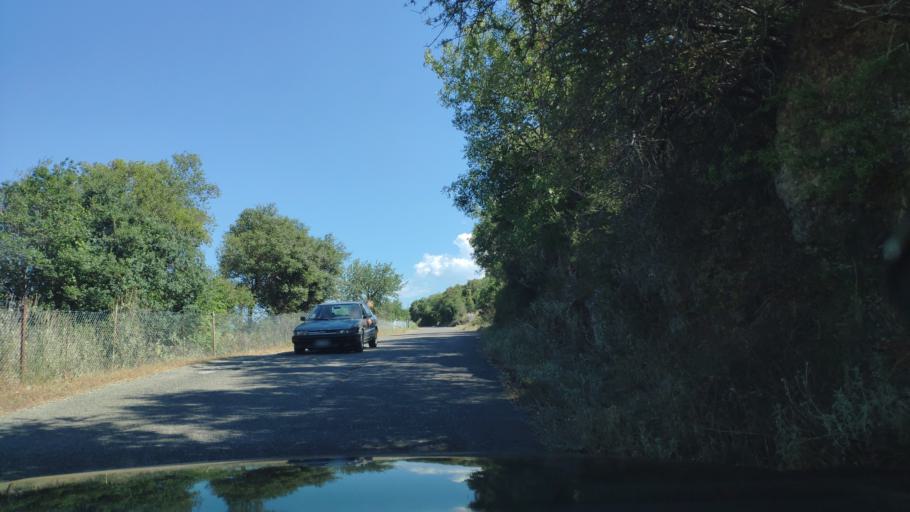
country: GR
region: West Greece
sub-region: Nomos Aitolias kai Akarnanias
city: Katouna
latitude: 38.8025
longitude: 21.1112
